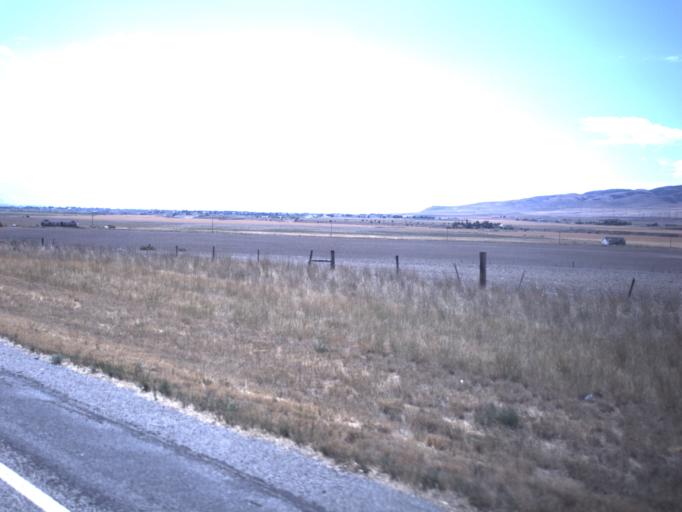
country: US
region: Utah
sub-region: Box Elder County
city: Garland
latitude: 41.8779
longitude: -112.1529
